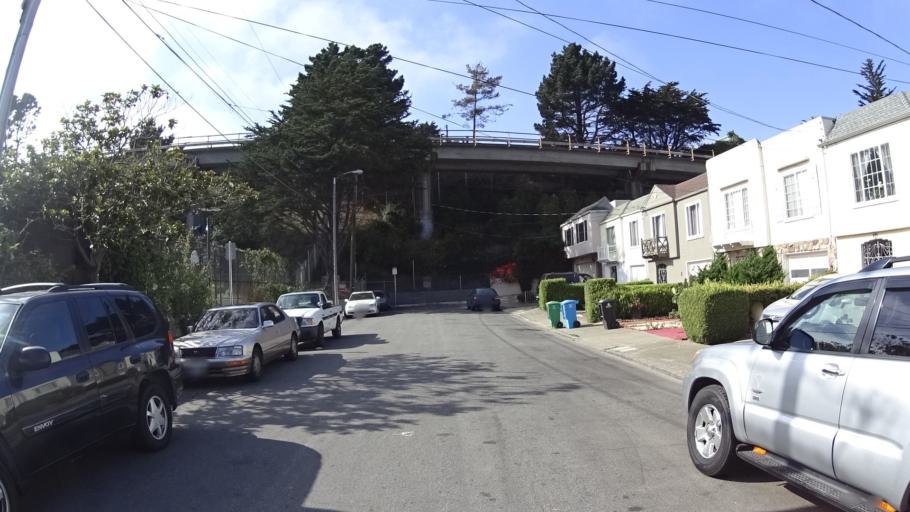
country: US
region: California
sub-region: San Mateo County
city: Daly City
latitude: 37.7144
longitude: -122.4495
